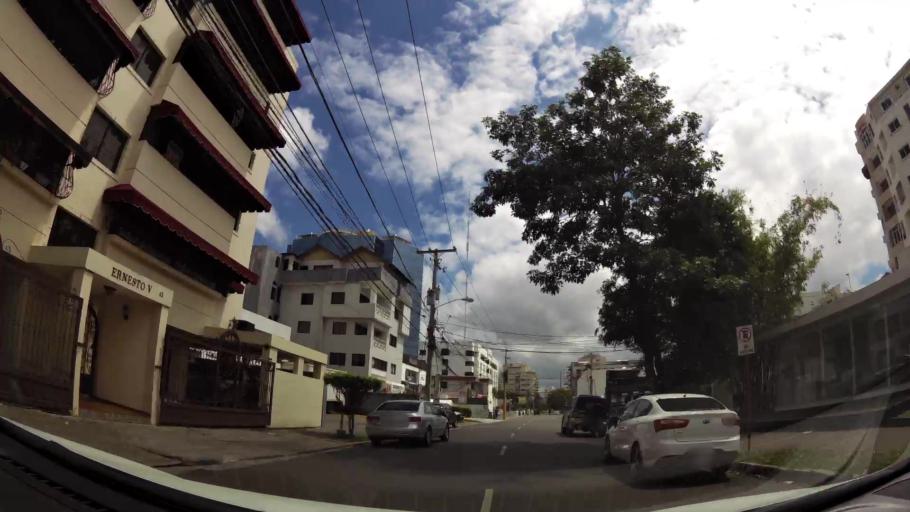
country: DO
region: Nacional
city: La Julia
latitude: 18.4723
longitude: -69.9326
